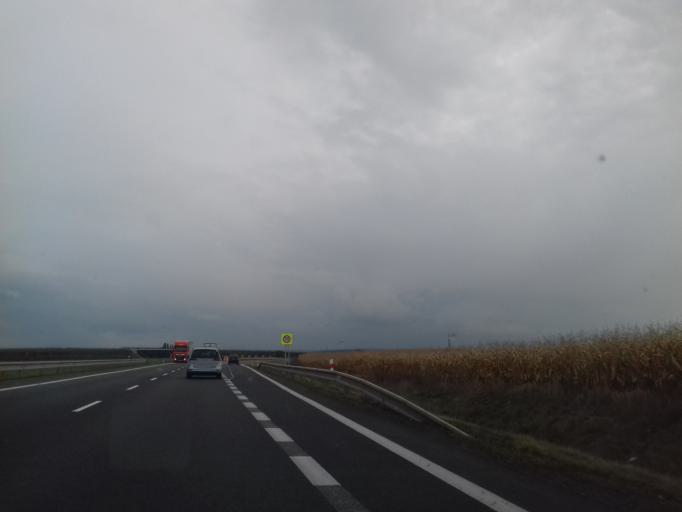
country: CZ
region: Pardubicky
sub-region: Okres Chrudim
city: Chrudim
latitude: 49.9799
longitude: 15.7795
